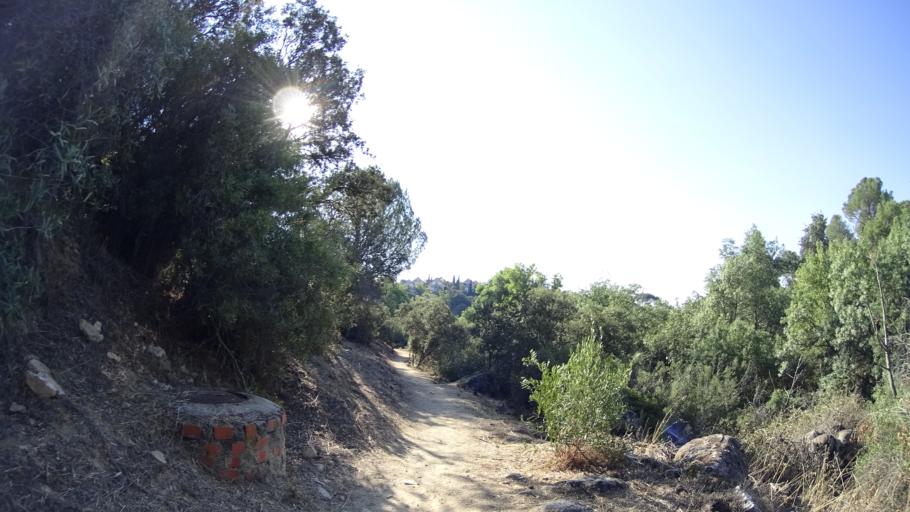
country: ES
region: Madrid
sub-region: Provincia de Madrid
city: Las Matas
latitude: 40.5813
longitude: -3.8963
